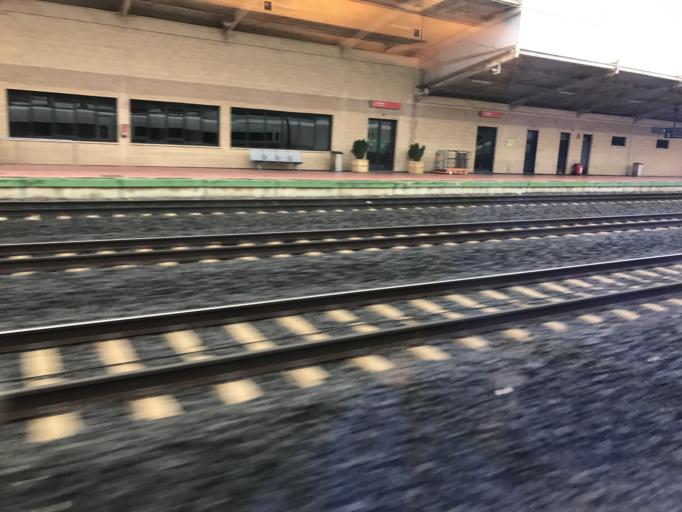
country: ES
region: Castille-La Mancha
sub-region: Provincia de Ciudad Real
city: Ciudad Real
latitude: 38.9850
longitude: -3.9130
